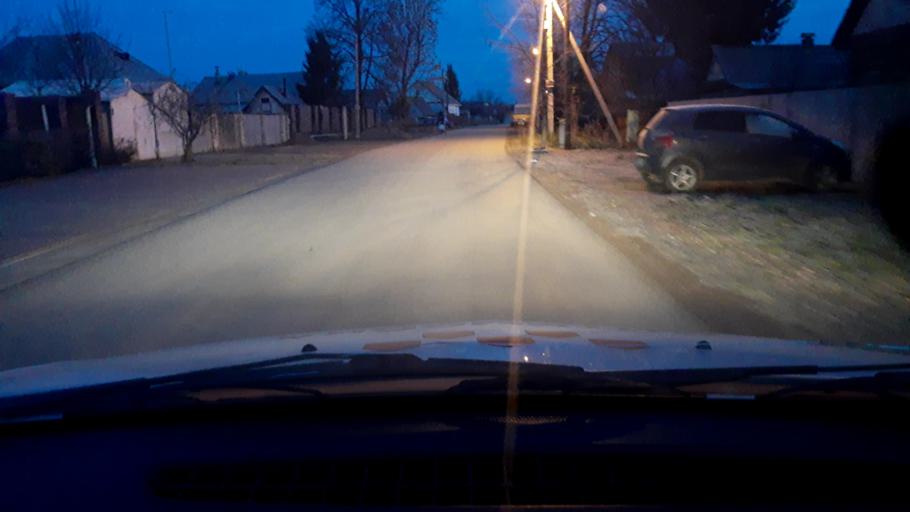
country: RU
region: Bashkortostan
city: Iglino
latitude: 54.7766
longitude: 56.2176
